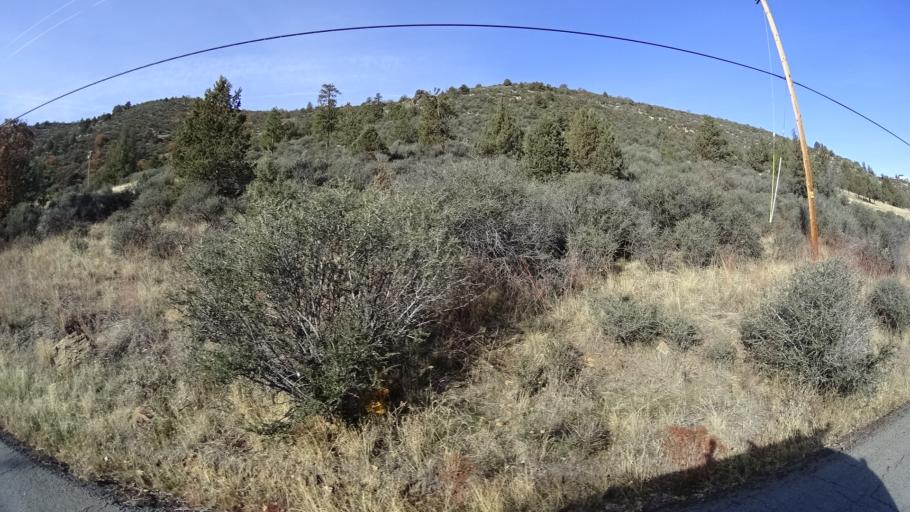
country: US
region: California
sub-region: Siskiyou County
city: Montague
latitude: 41.6204
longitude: -122.5770
